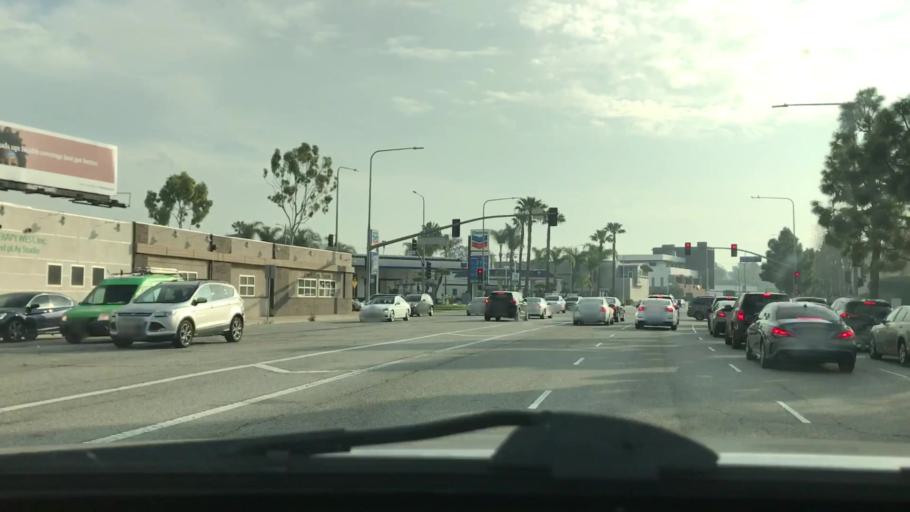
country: US
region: California
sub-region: Los Angeles County
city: Ladera Heights
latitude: 33.9839
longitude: -118.4018
